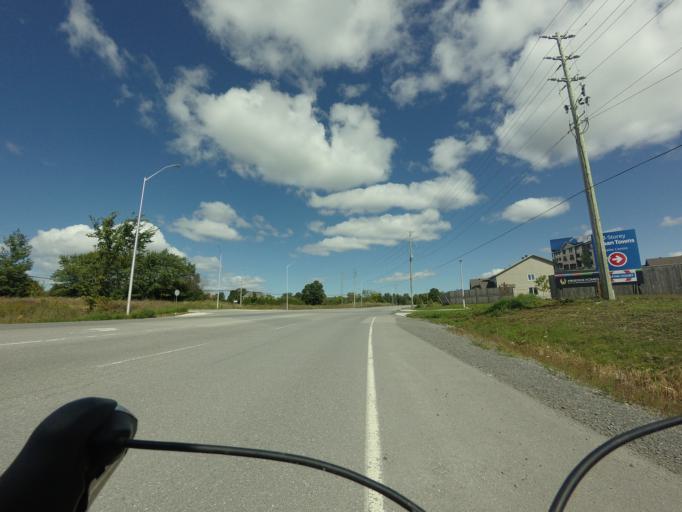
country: CA
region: Ontario
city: Bells Corners
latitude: 45.2753
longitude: -75.7861
